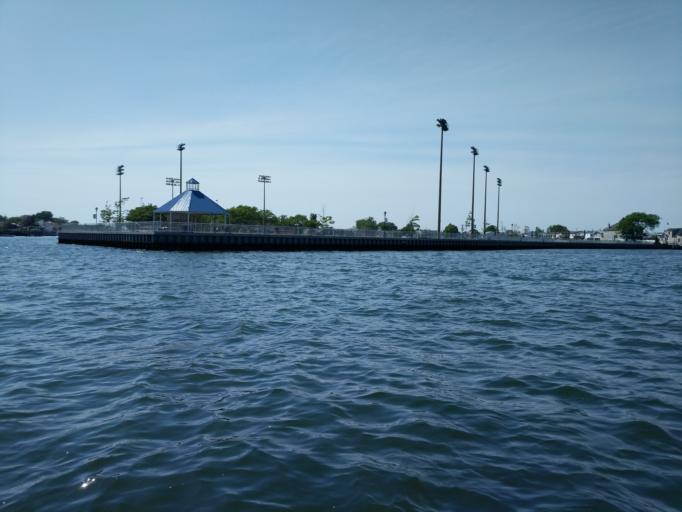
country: US
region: New York
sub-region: Nassau County
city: Barnum Island
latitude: 40.5988
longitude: -73.6444
